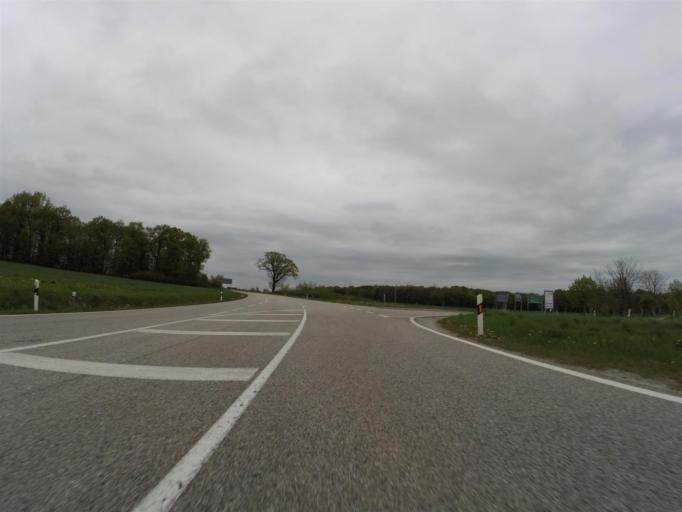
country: DE
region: Saxony-Anhalt
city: Naumburg
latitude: 51.1084
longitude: 11.7721
